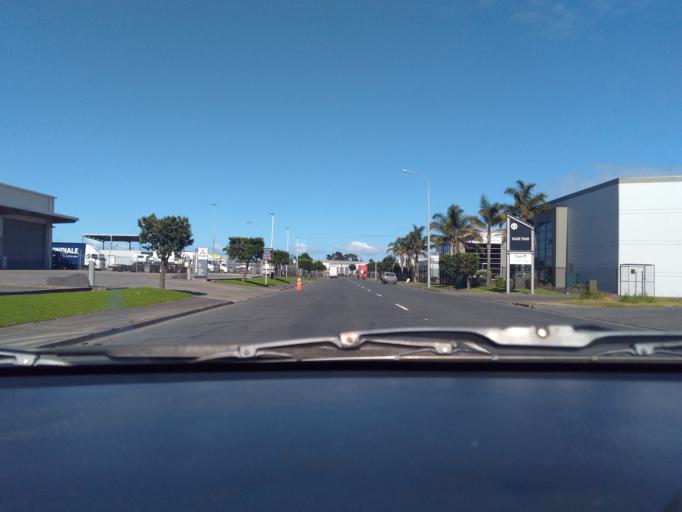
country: NZ
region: Auckland
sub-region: Auckland
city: Wiri
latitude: -37.0022
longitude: 174.8520
